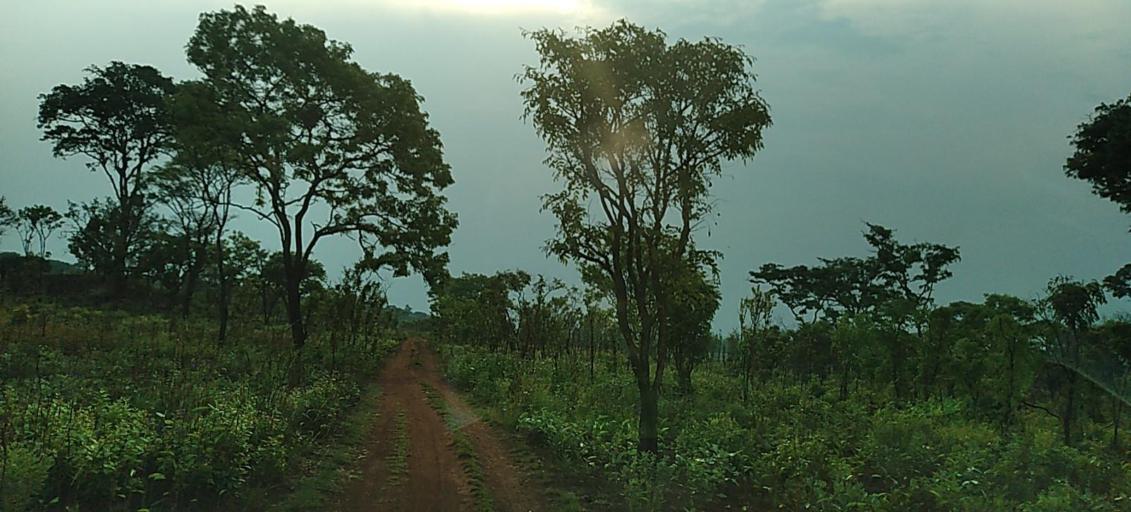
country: ZM
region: North-Western
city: Solwezi
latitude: -12.0427
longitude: 26.0303
